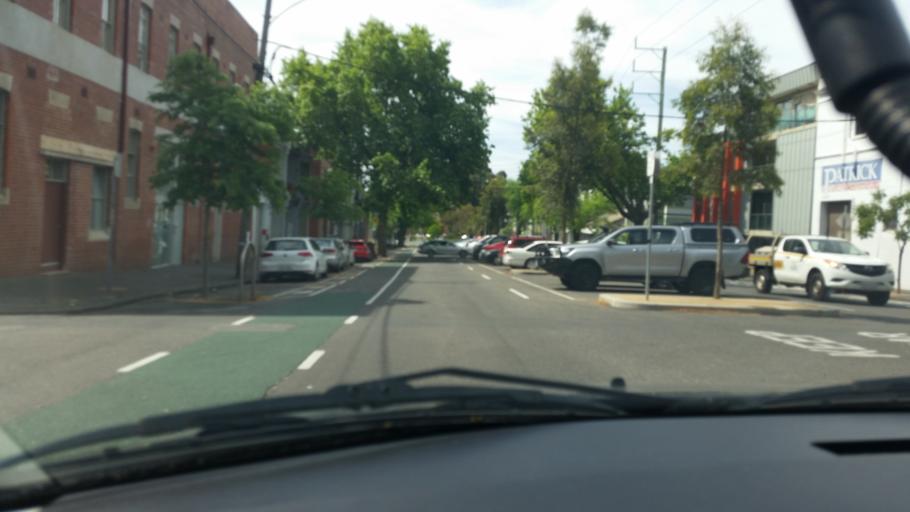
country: AU
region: Victoria
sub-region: Melbourne
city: North Melbourne
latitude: -37.8022
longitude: 144.9512
